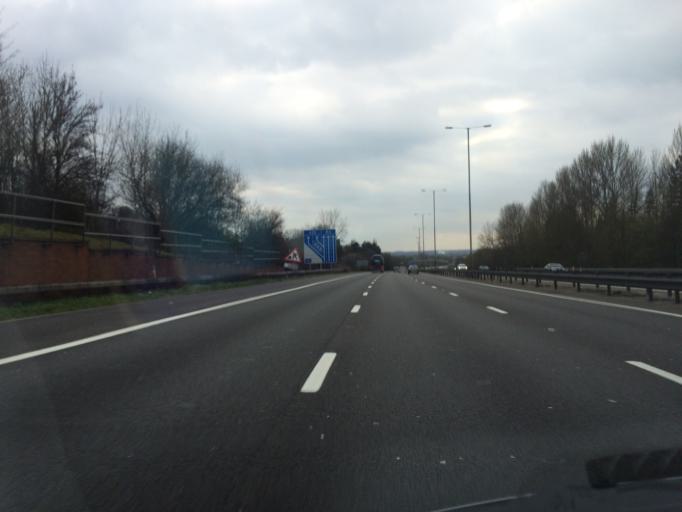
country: GB
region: England
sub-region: Wokingham
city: Shinfield
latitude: 51.4141
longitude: -0.9503
